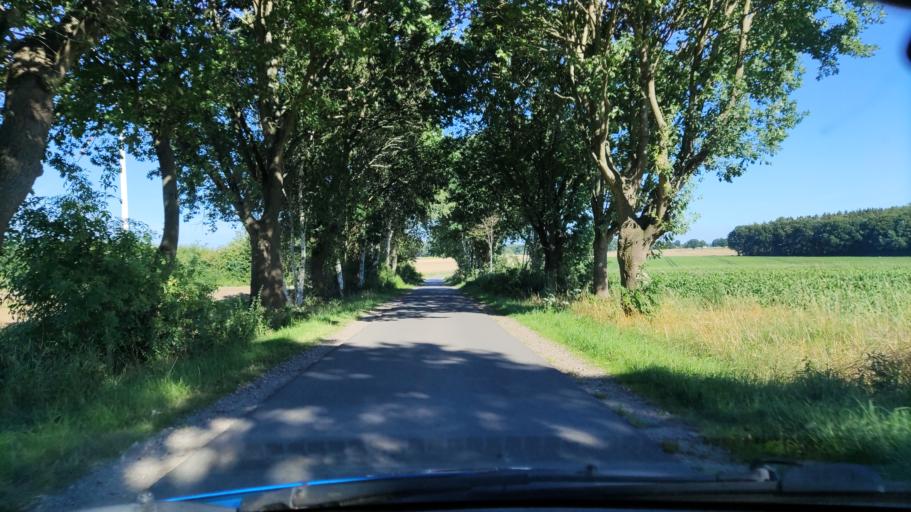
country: DE
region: Lower Saxony
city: Nahrendorf
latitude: 53.1787
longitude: 10.7959
